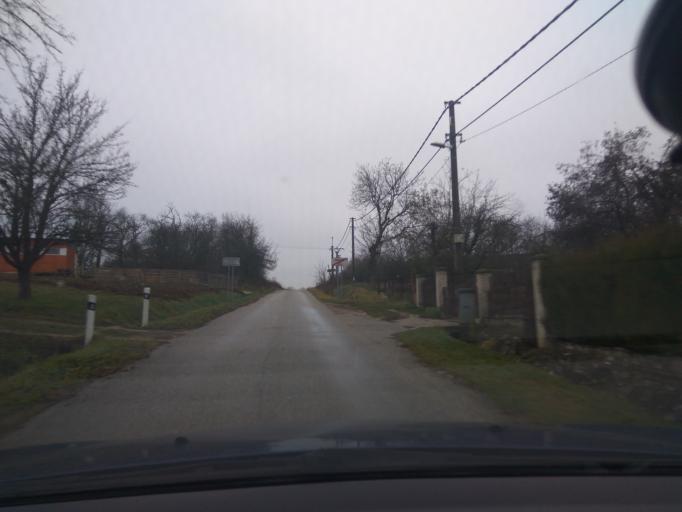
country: SK
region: Trnavsky
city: Vrbove
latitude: 48.6755
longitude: 17.6819
